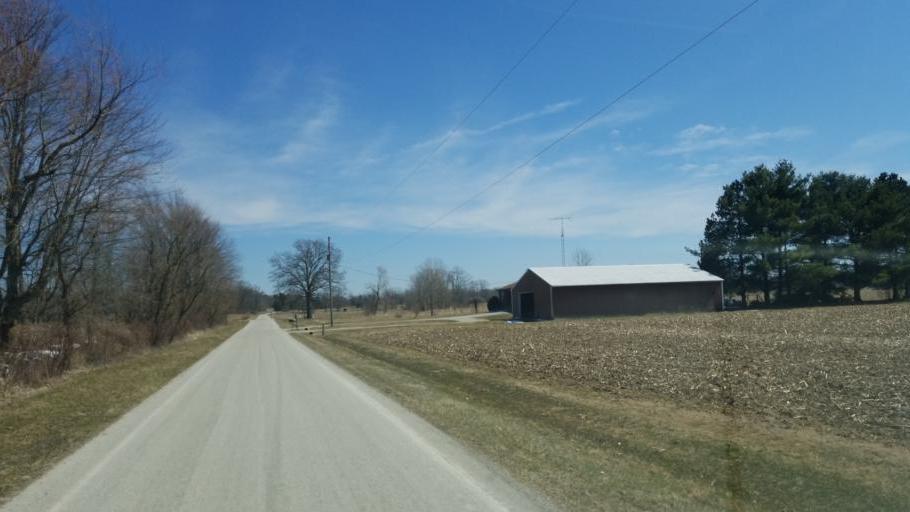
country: US
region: Ohio
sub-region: Crawford County
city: Galion
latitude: 40.6616
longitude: -82.8097
